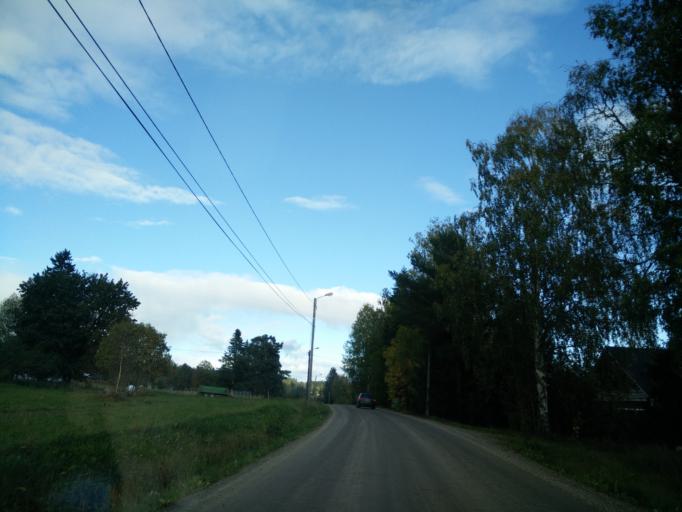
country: SE
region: Vaesternorrland
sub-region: Sundsvalls Kommun
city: Matfors
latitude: 62.3339
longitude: 16.9584
